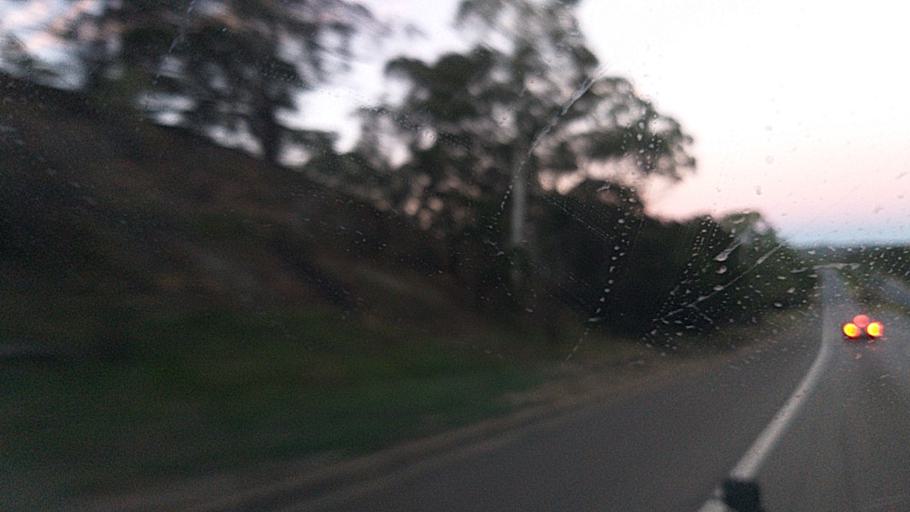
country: AU
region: New South Wales
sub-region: Wingecarribee
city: Bundanoon
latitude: -34.6518
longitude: 150.0907
